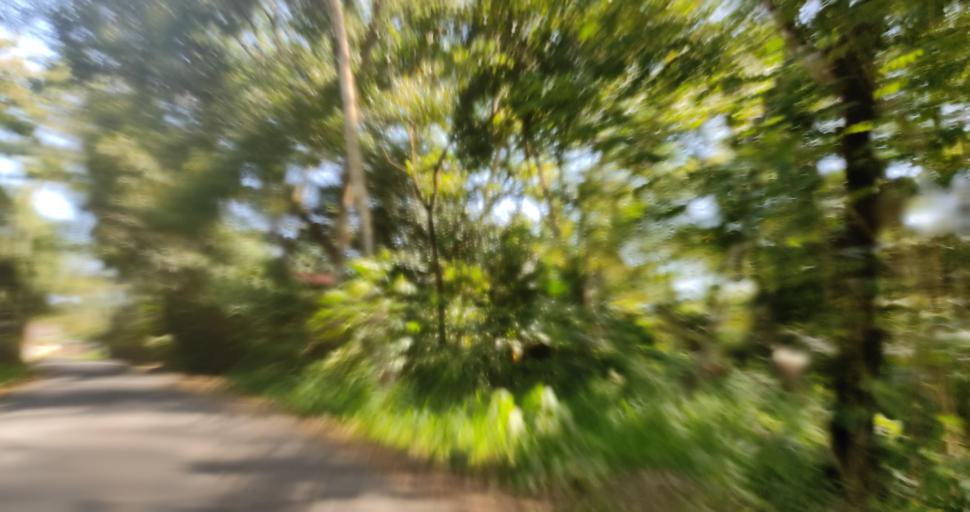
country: IN
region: Kerala
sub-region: Alappuzha
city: Shertallai
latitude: 9.6271
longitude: 76.3434
